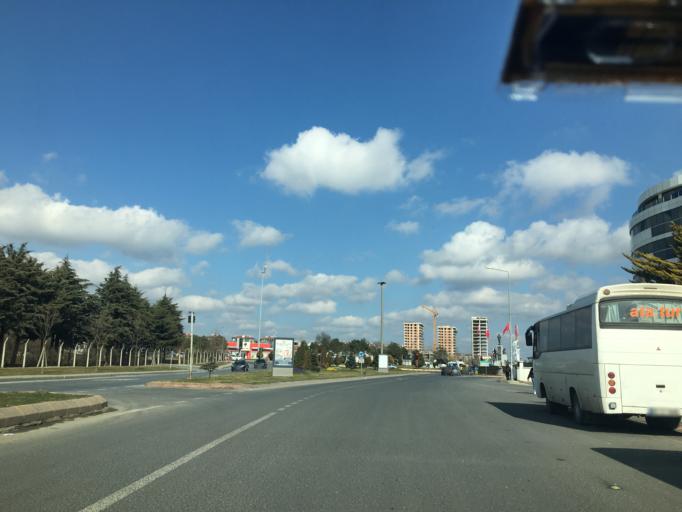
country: TR
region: Tekirdag
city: Cerkezkoey
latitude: 41.2952
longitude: 27.9961
